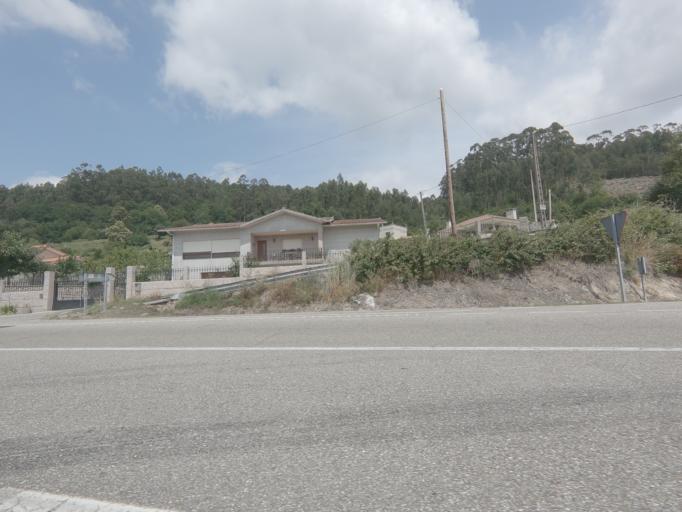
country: ES
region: Galicia
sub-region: Provincia de Pontevedra
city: Tomino
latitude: 42.0398
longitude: -8.7276
